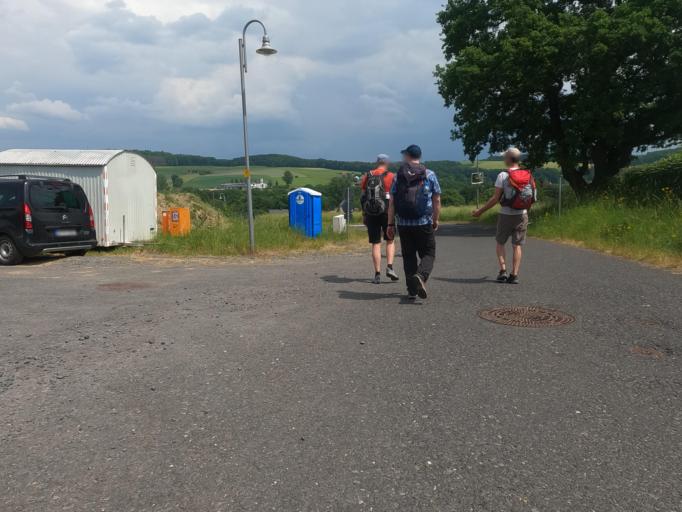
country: DE
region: Rheinland-Pfalz
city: Enspel
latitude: 50.6339
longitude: 7.8891
